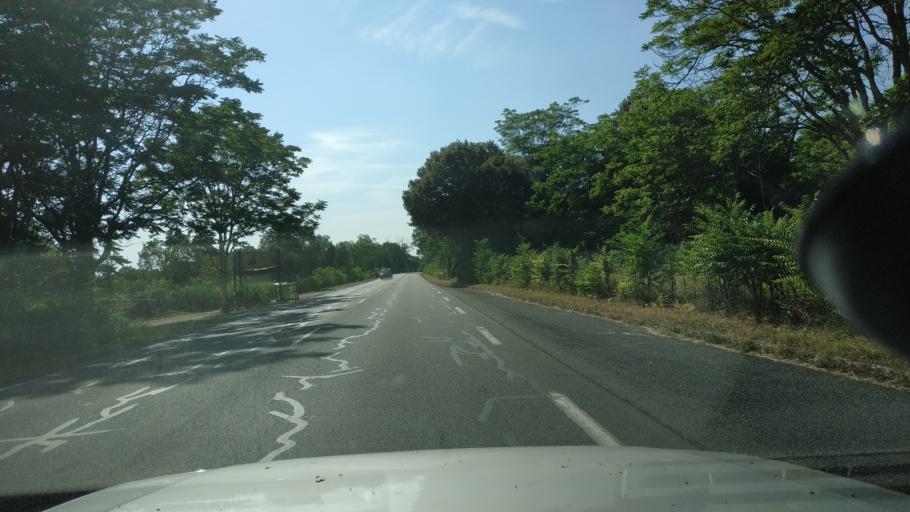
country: FR
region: Midi-Pyrenees
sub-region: Departement du Lot
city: Gramat
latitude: 44.7954
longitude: 1.6897
